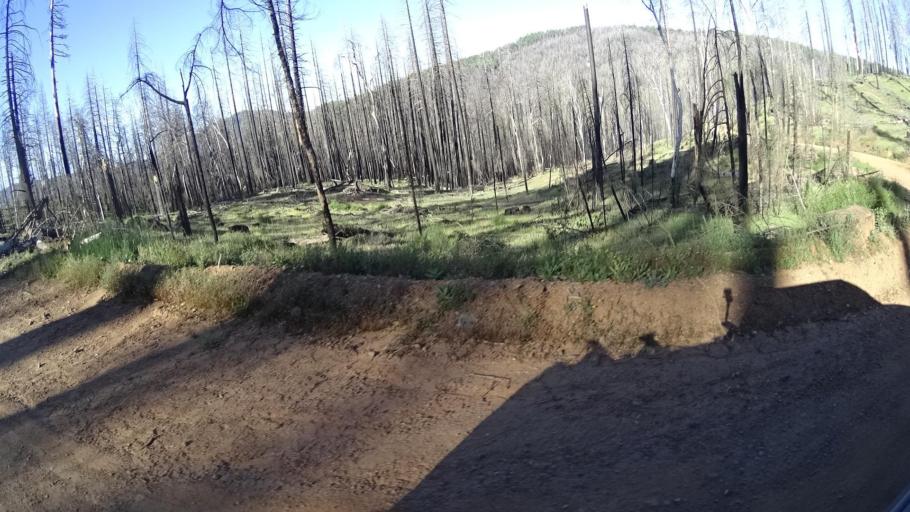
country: US
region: California
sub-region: Lake County
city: Upper Lake
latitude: 39.3597
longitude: -122.9907
